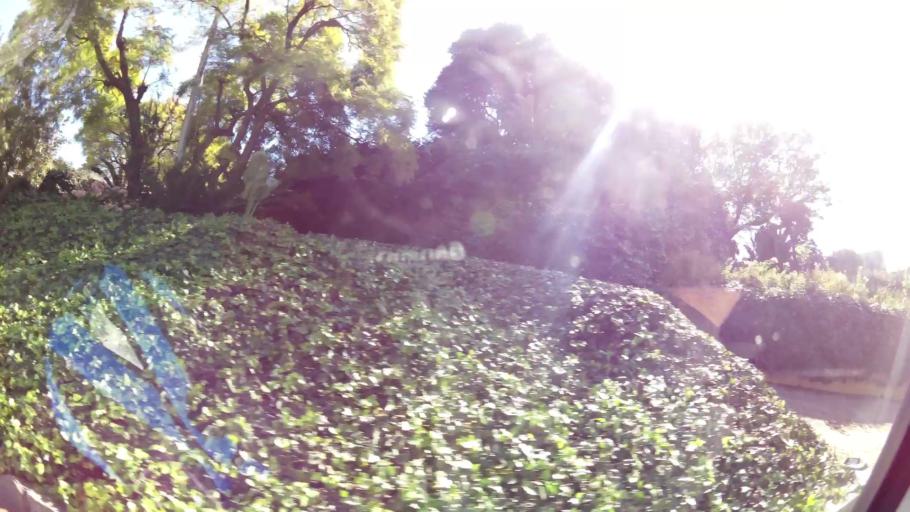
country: ZA
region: Gauteng
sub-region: City of Tshwane Metropolitan Municipality
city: Pretoria
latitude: -25.7878
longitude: 28.2447
